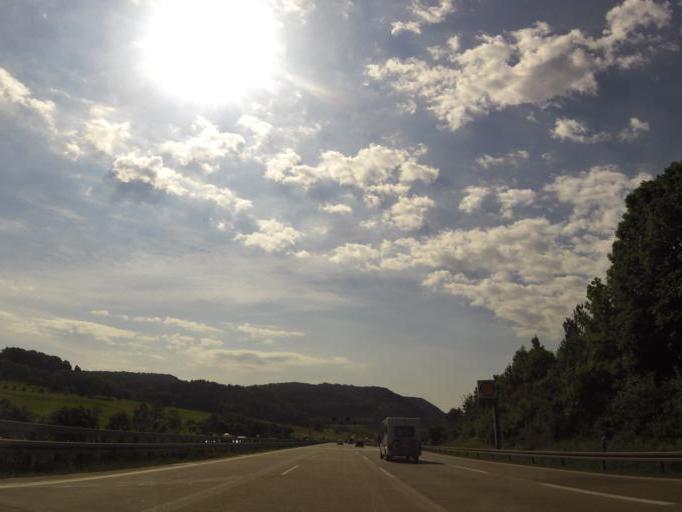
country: DE
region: Baden-Wuerttemberg
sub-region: Regierungsbezirk Stuttgart
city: Gruibingen
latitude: 48.6091
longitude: 9.6282
